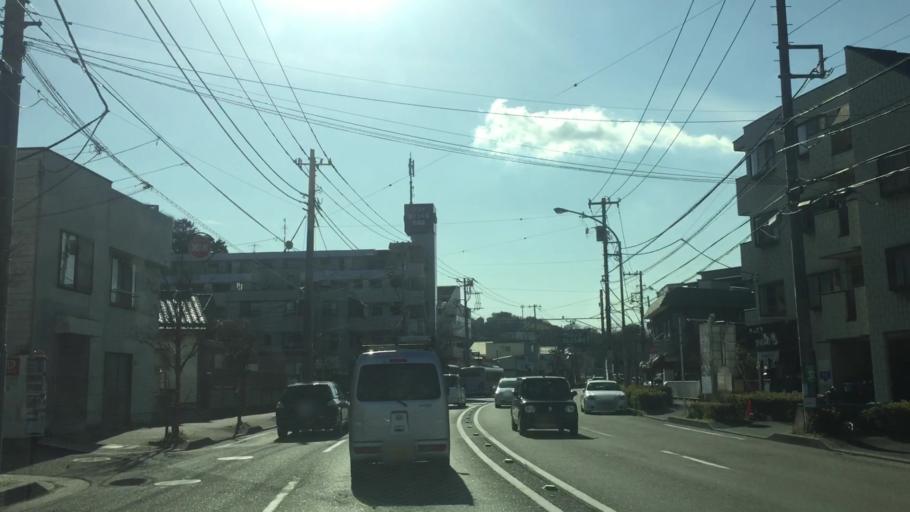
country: JP
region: Kanagawa
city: Zushi
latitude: 35.3674
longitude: 139.6134
